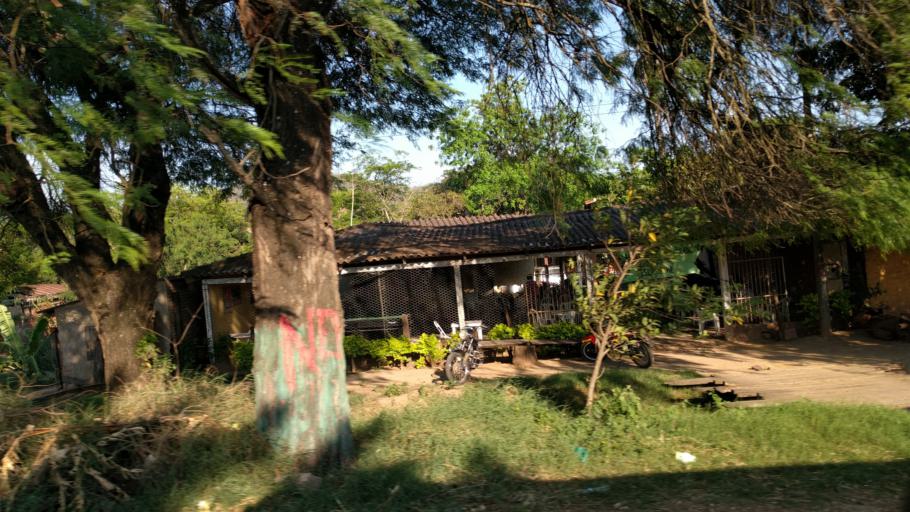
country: BO
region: Santa Cruz
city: Jorochito
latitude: -18.1125
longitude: -63.4593
